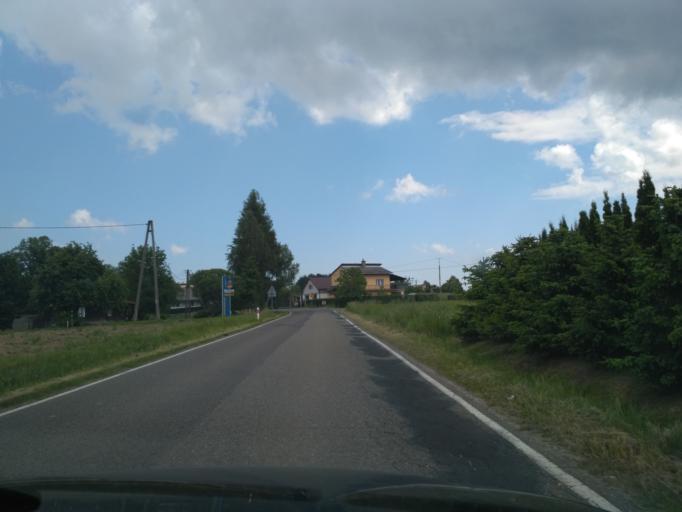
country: PL
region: Subcarpathian Voivodeship
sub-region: Powiat rzeszowski
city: Hyzne
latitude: 49.9346
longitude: 22.1890
